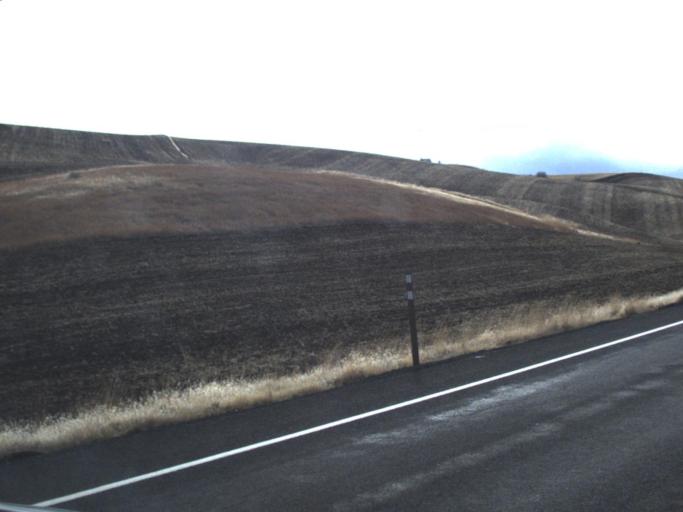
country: US
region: Washington
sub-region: Whitman County
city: Colfax
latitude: 46.8269
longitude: -117.5224
